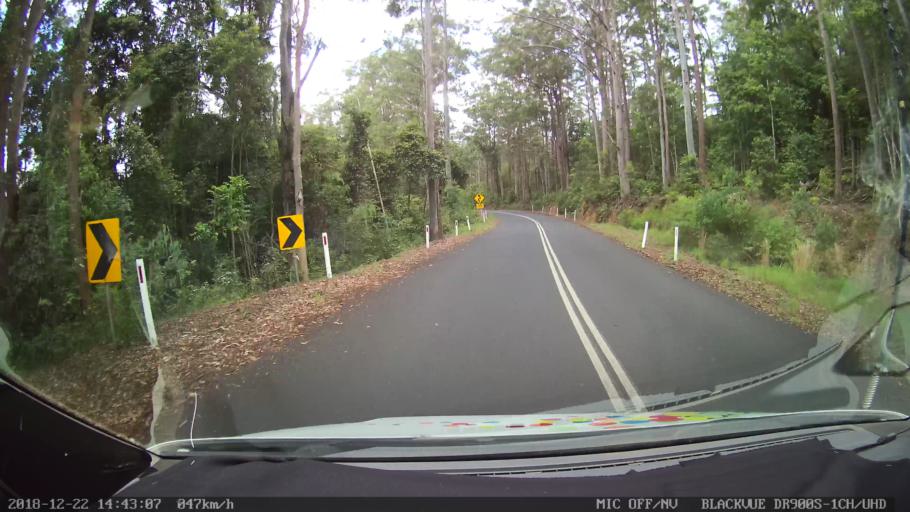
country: AU
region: New South Wales
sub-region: Bellingen
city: Dorrigo
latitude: -30.1644
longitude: 152.5857
